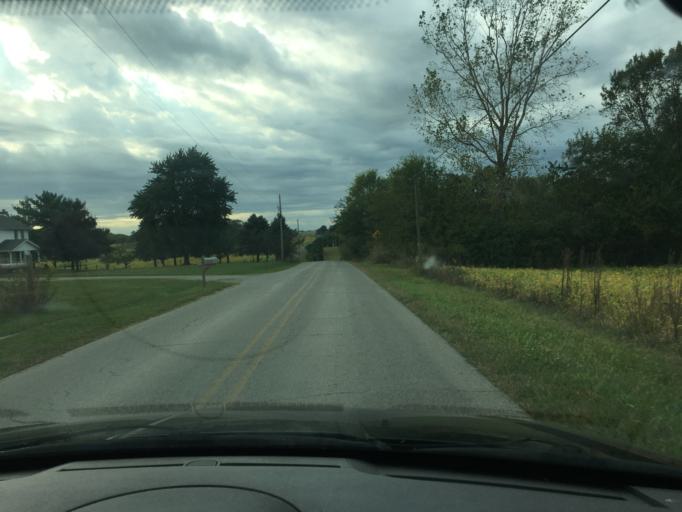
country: US
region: Ohio
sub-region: Logan County
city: Bellefontaine
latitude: 40.3346
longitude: -83.8025
